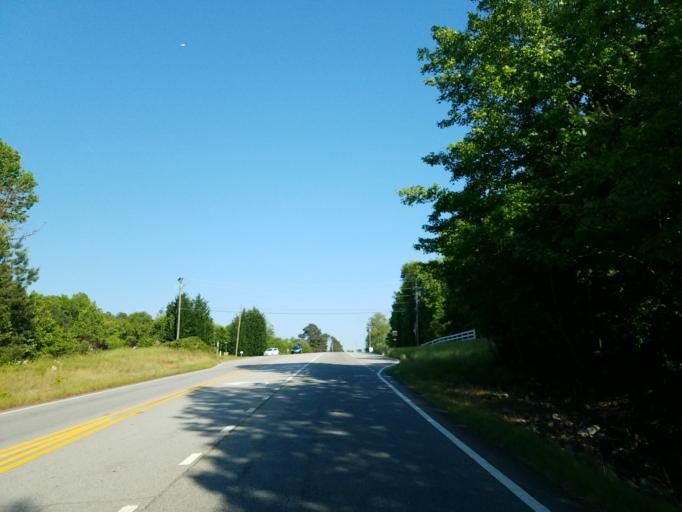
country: US
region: Georgia
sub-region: Carroll County
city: Villa Rica
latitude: 33.7643
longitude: -84.9511
